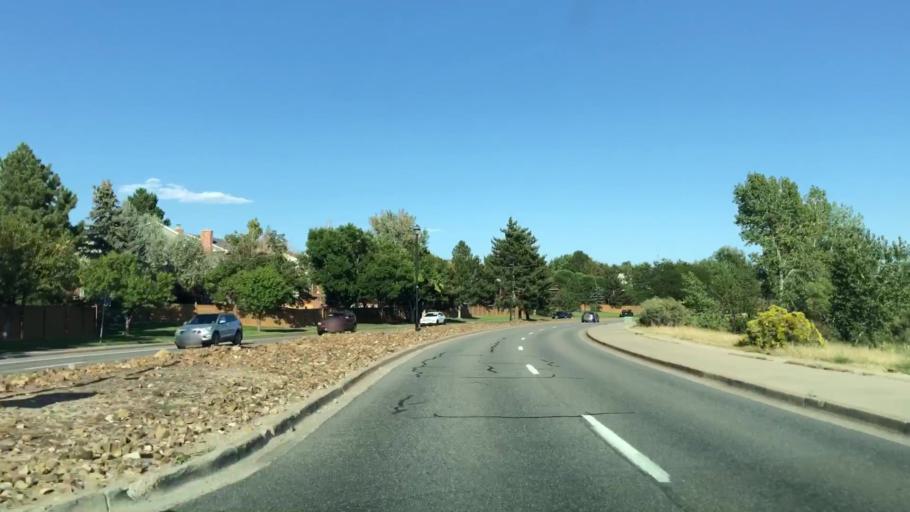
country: US
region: Colorado
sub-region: Arapahoe County
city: Dove Valley
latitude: 39.6117
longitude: -104.7974
